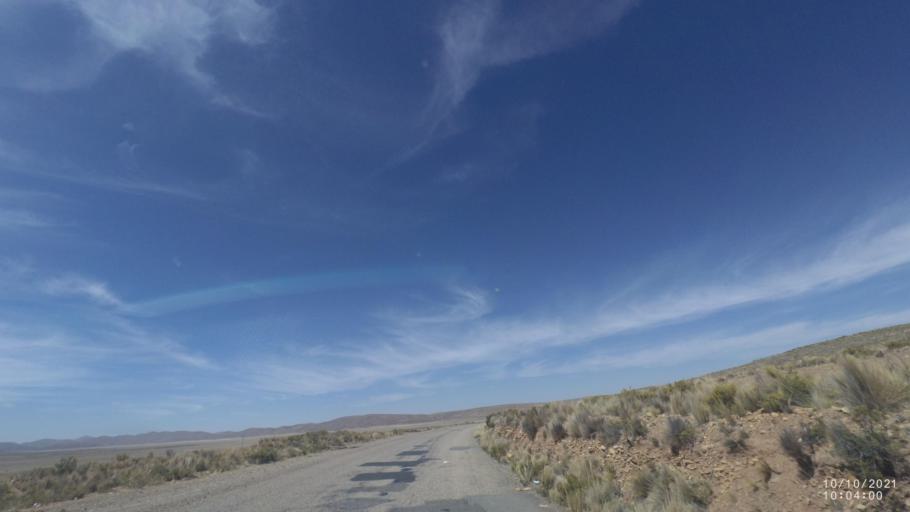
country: BO
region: La Paz
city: Eucaliptus
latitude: -17.3778
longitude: -67.4417
